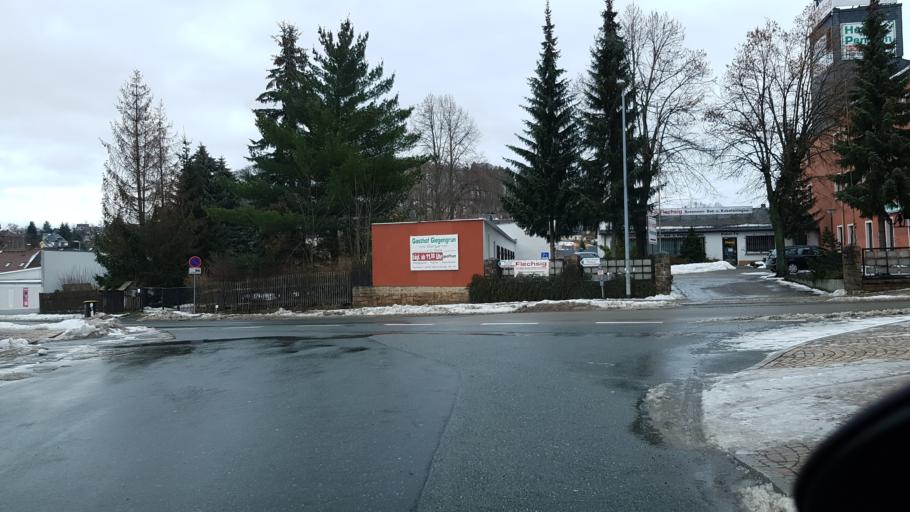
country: DE
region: Saxony
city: Kirchberg
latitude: 50.6214
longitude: 12.5205
